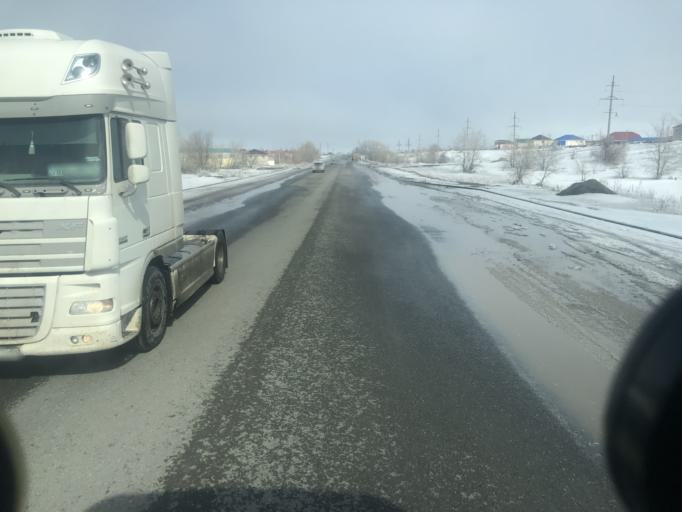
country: KZ
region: Aqtoebe
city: Aqtobe
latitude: 50.2827
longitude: 57.2830
